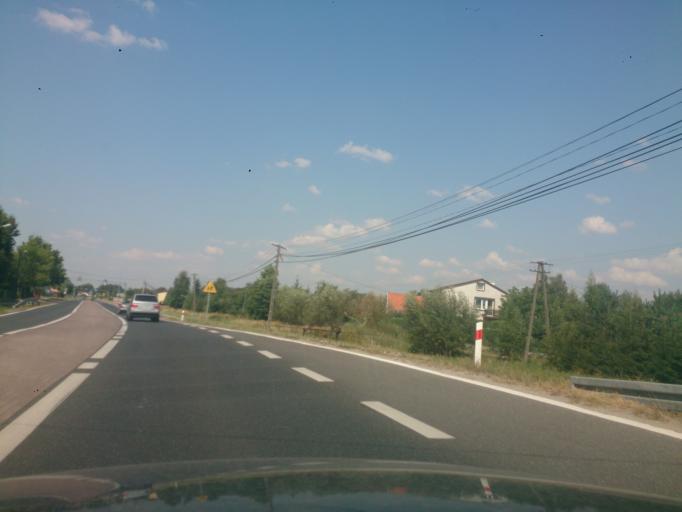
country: PL
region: Subcarpathian Voivodeship
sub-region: Powiat kolbuszowski
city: Kolbuszowa
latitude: 50.2239
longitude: 21.7979
